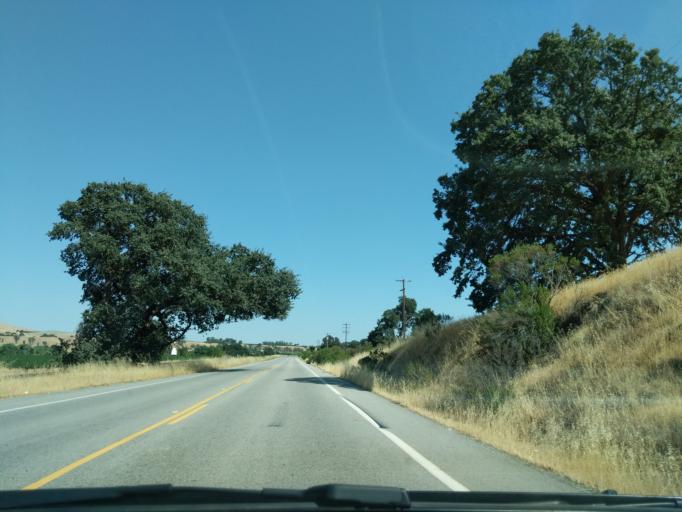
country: US
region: California
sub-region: San Luis Obispo County
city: San Miguel
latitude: 35.7682
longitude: -120.7015
